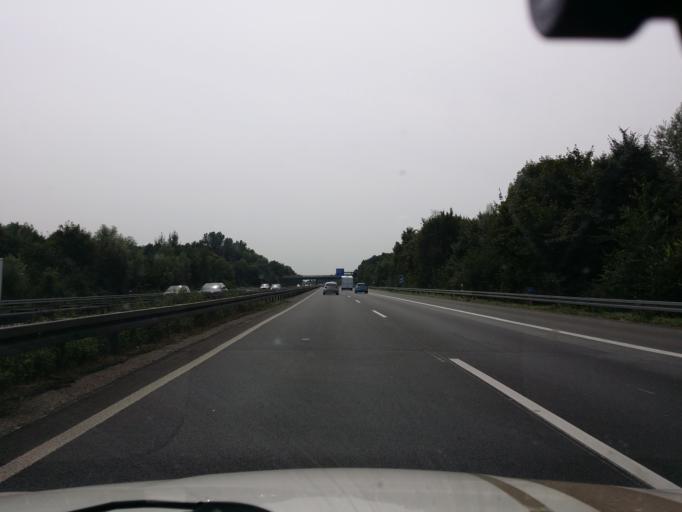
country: DE
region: Hesse
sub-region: Regierungsbezirk Darmstadt
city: Alsbach-Hahnlein
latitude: 49.7263
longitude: 8.5931
